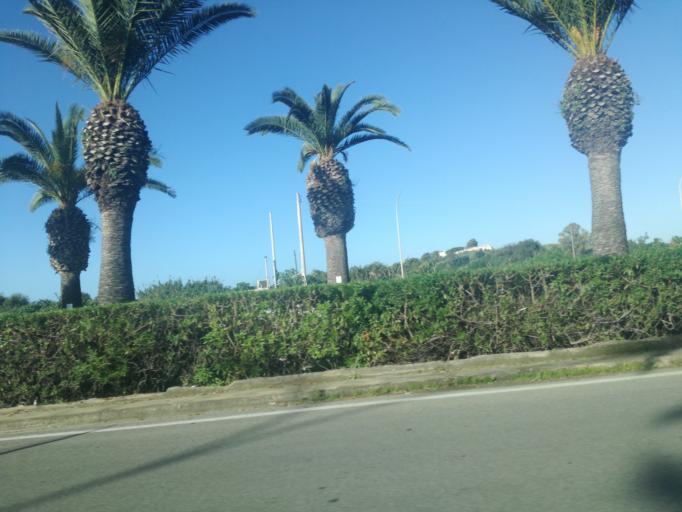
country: IT
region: Sicily
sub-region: Provincia di Caltanissetta
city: Gela
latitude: 37.0597
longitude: 14.2655
